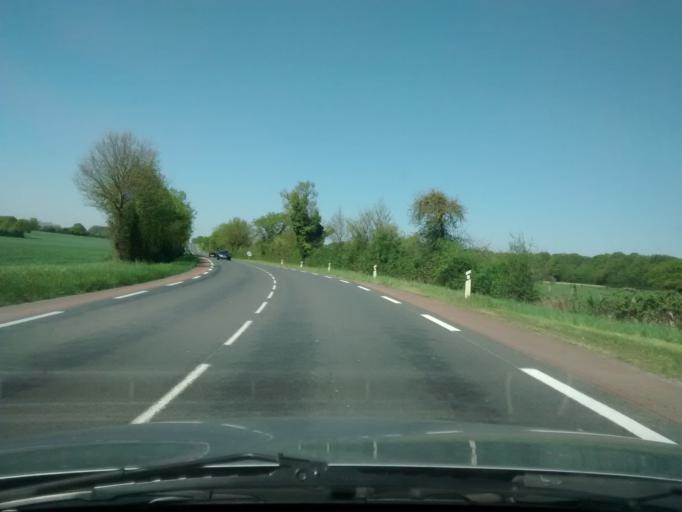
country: FR
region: Pays de la Loire
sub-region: Departement de la Sarthe
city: Brulon
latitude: 48.0307
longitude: -0.2932
